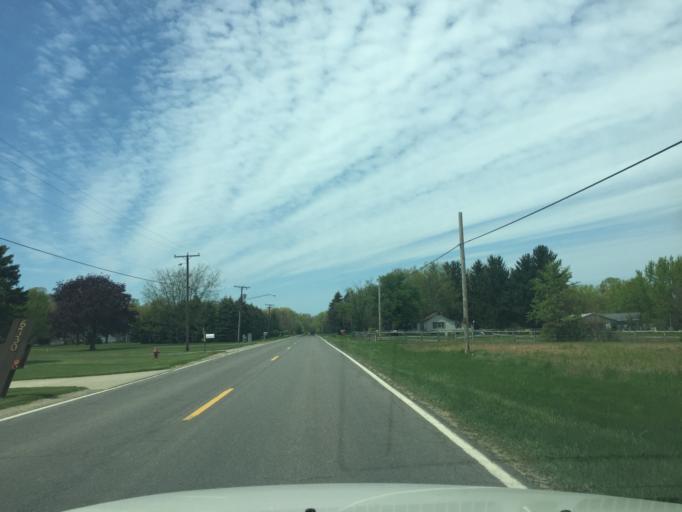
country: US
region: Michigan
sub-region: Berrien County
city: Stevensville
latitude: 41.9957
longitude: -86.5102
